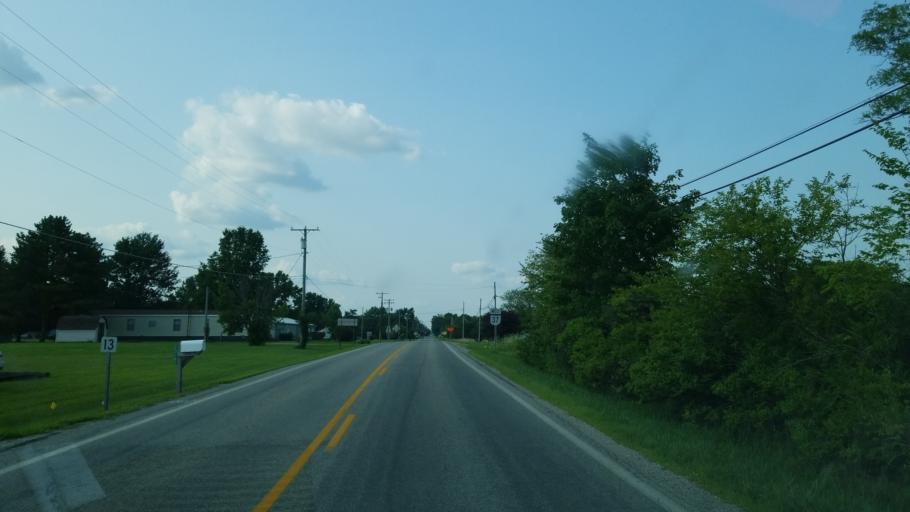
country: US
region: Ohio
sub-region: Union County
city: Richwood
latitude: 40.3454
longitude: -83.2646
